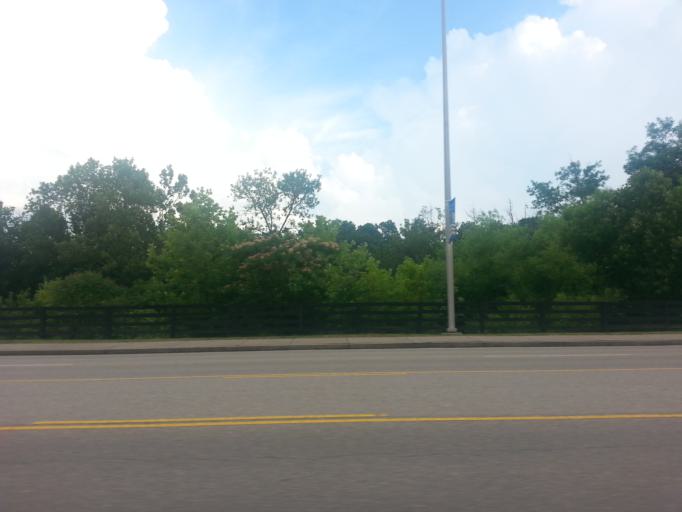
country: US
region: Tennessee
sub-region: Knox County
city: Farragut
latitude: 35.8766
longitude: -84.1492
